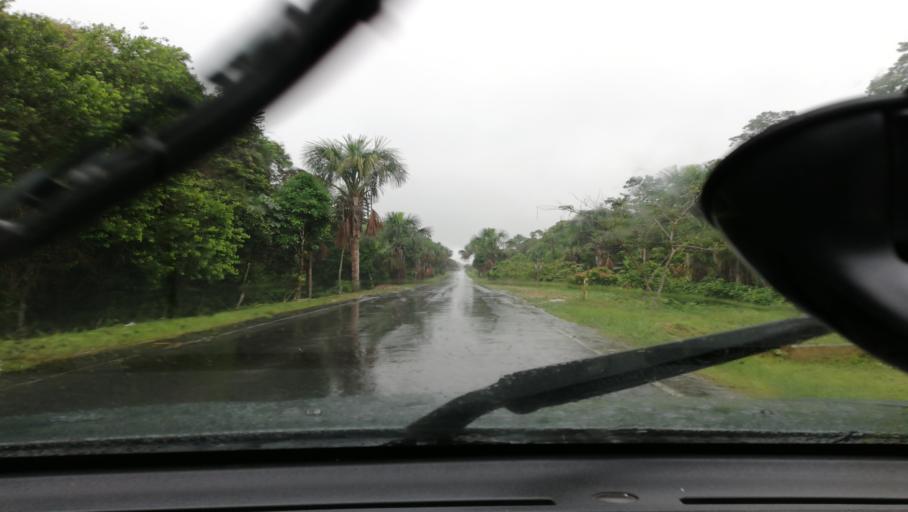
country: PE
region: Loreto
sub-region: Provincia de Maynas
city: San Juan
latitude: -3.9512
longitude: -73.4048
